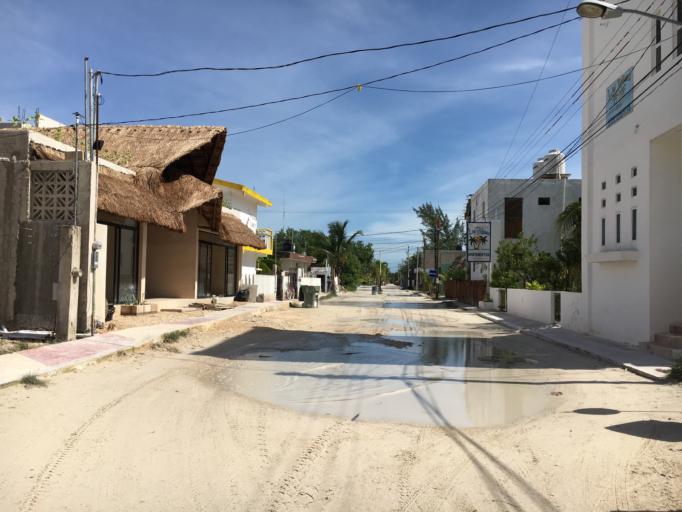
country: MX
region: Quintana Roo
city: Kantunilkin
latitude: 21.5224
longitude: -87.3776
